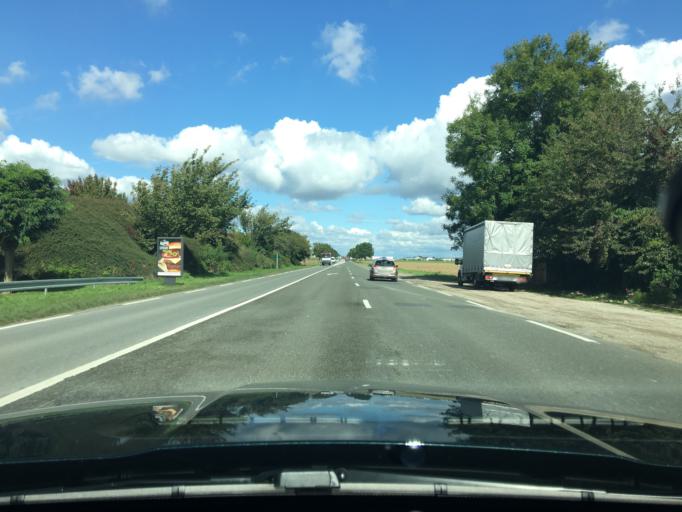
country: FR
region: Ile-de-France
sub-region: Departement du Val-d'Oise
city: Louvres
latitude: 49.0500
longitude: 2.5131
